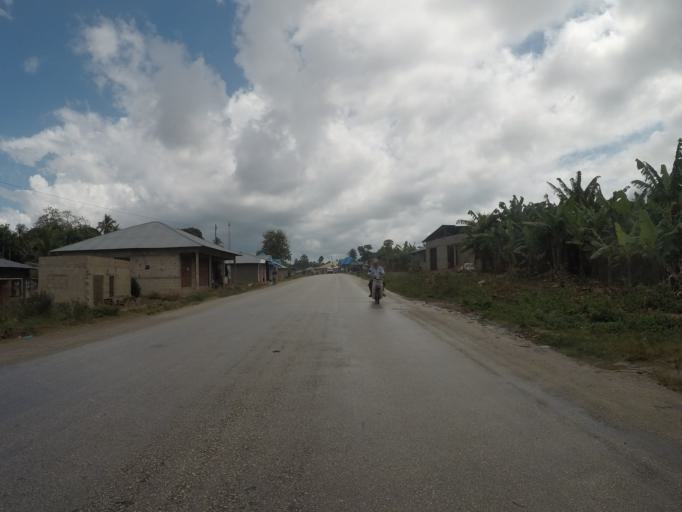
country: TZ
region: Zanzibar Central/South
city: Koani
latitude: -6.0382
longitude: 39.2315
